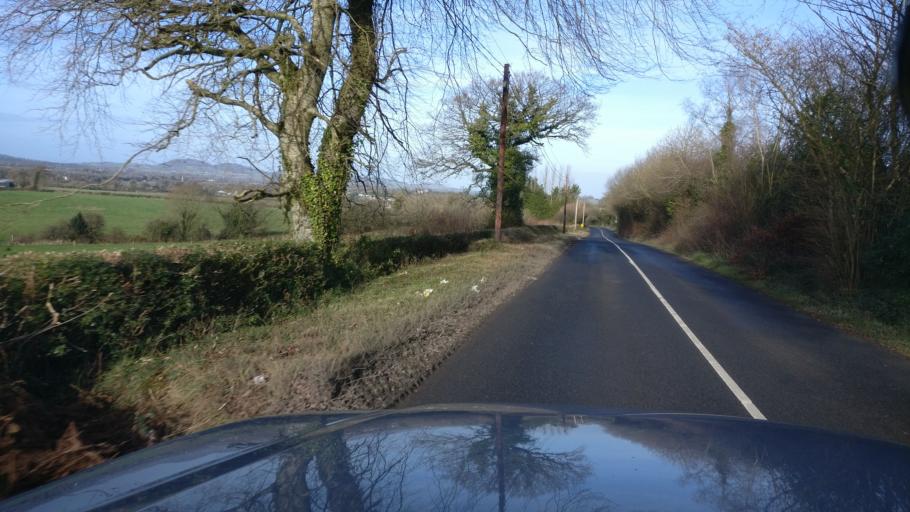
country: IE
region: Leinster
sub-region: Laois
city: Stradbally
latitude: 52.9482
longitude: -7.1996
